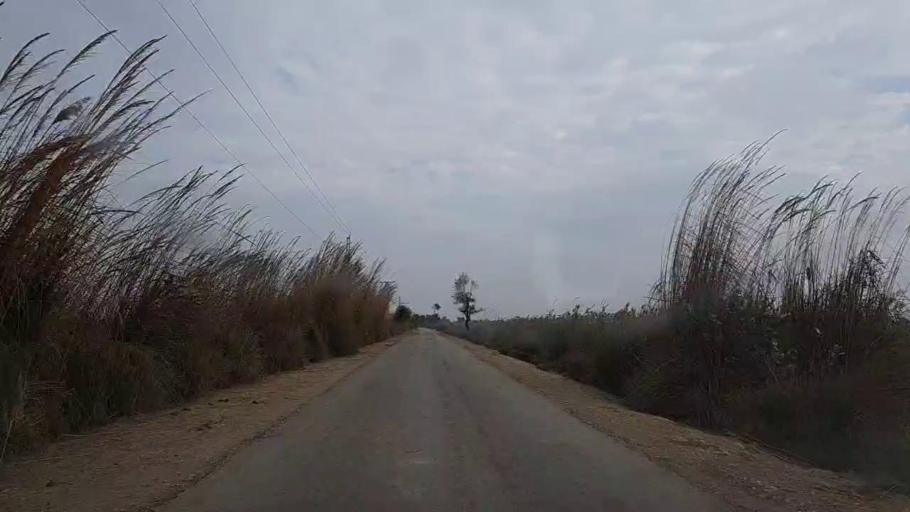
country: PK
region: Sindh
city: Sanghar
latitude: 26.2308
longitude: 68.9872
